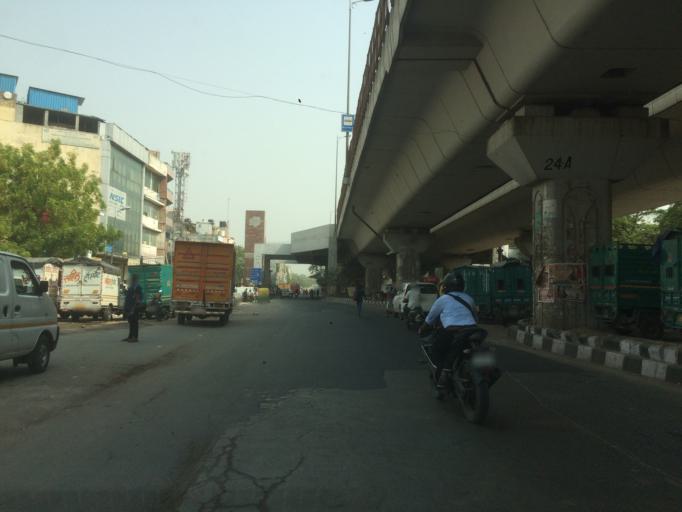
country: IN
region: NCT
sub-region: Central Delhi
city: Karol Bagh
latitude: 28.6247
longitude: 77.1347
